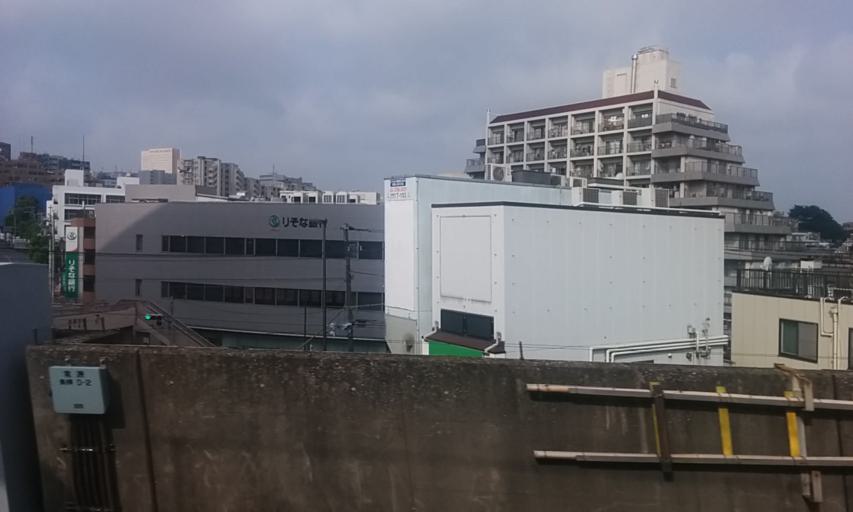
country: JP
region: Kanagawa
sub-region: Kawasaki-shi
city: Kawasaki
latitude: 35.6100
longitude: 139.7428
